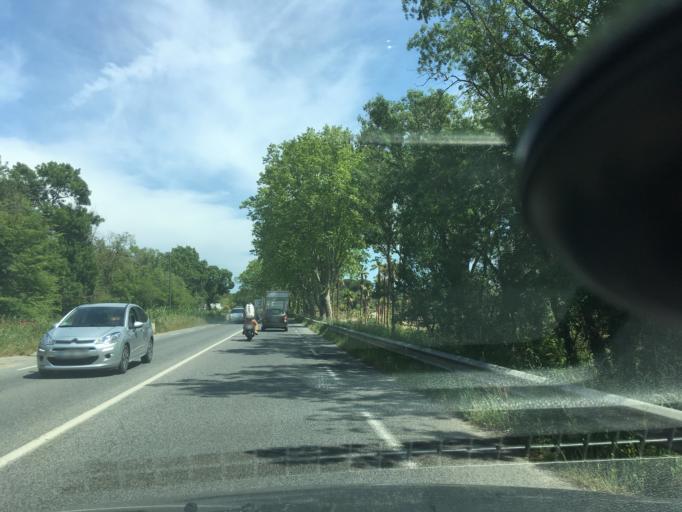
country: FR
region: Provence-Alpes-Cote d'Azur
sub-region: Departement du Var
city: Roquebrune-sur-Argens
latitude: 43.4619
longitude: 6.6515
